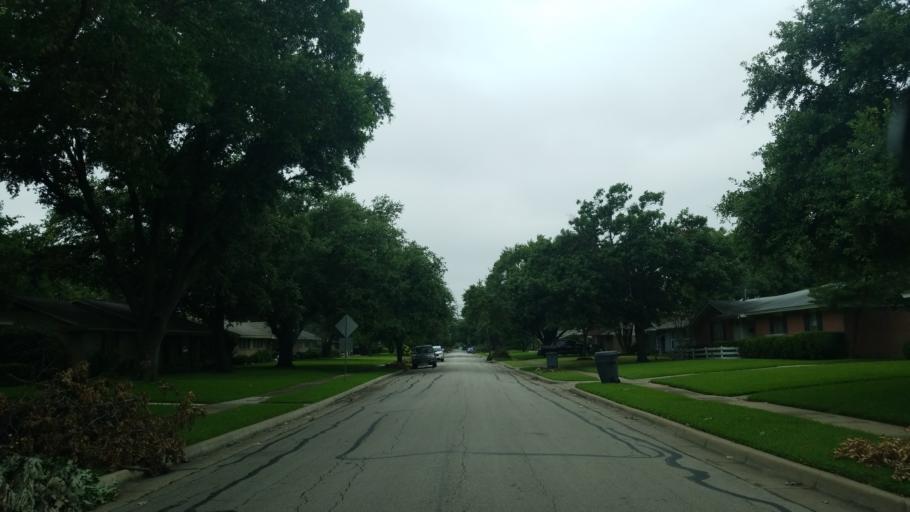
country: US
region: Texas
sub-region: Dallas County
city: Farmers Branch
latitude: 32.8988
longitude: -96.8661
